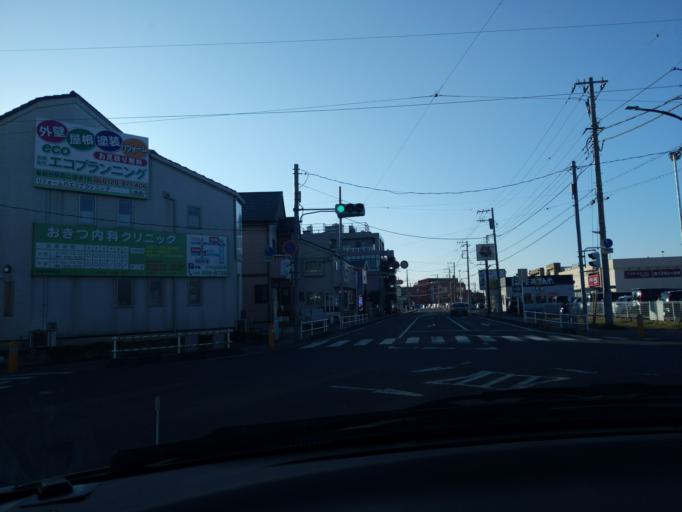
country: JP
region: Saitama
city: Koshigaya
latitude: 35.8750
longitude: 139.7849
